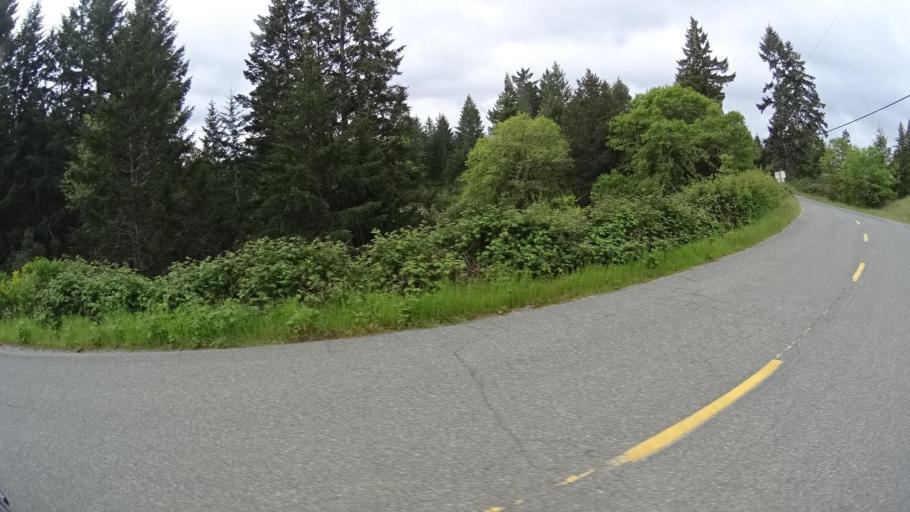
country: US
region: California
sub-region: Humboldt County
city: Redway
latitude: 40.2941
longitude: -123.8188
